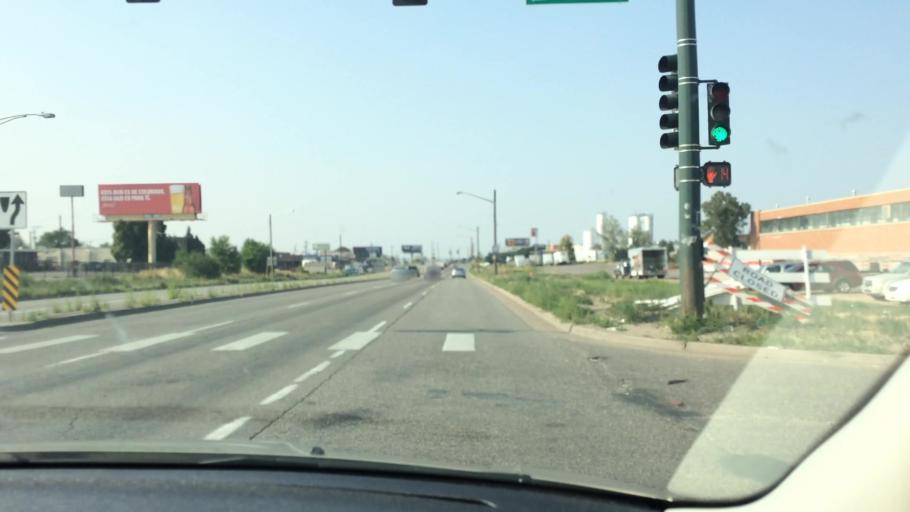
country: US
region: Colorado
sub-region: Adams County
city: Commerce City
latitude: 39.7838
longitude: -104.9404
